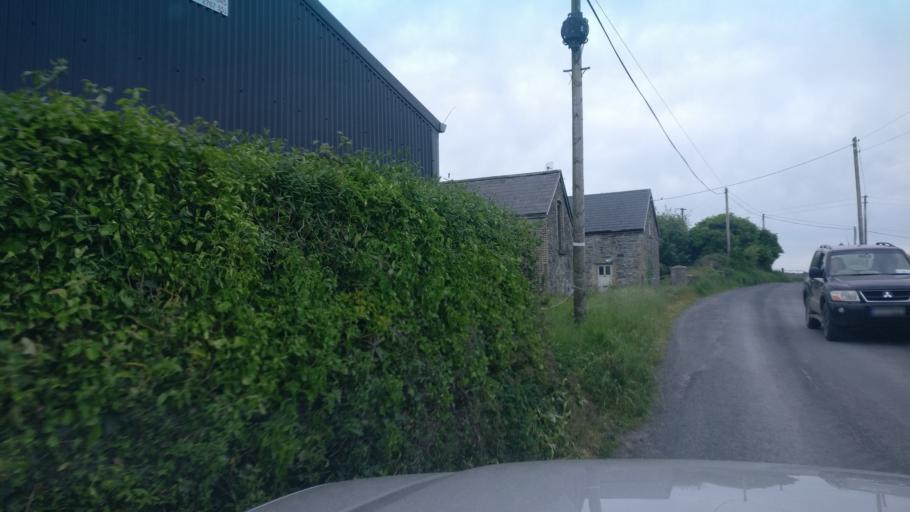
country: IE
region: Connaught
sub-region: County Galway
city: Portumna
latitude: 53.1451
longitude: -8.2875
